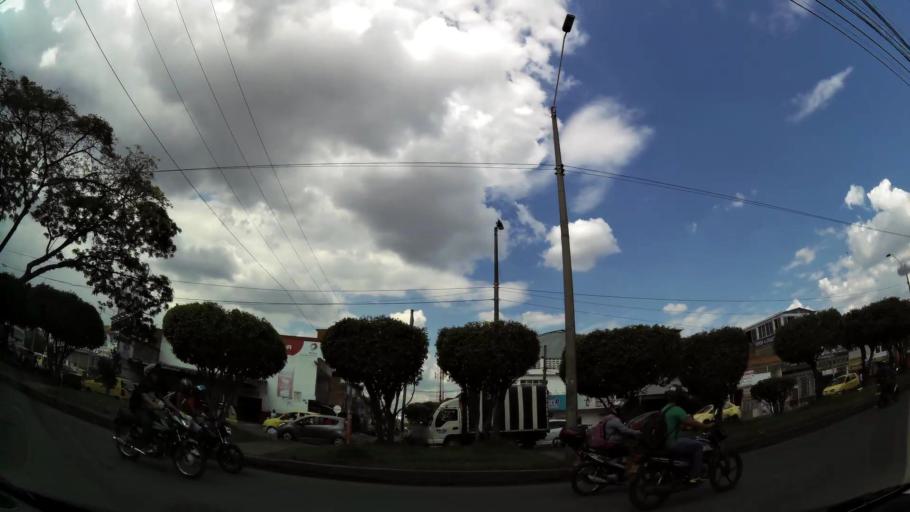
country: CO
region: Valle del Cauca
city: Cali
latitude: 3.4091
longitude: -76.5178
